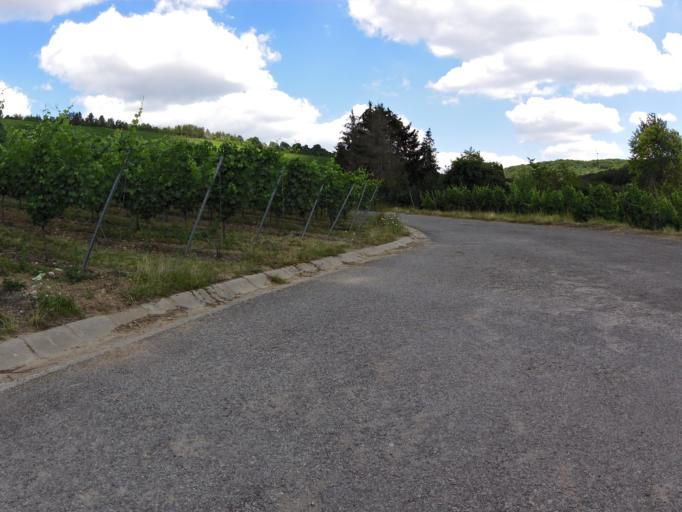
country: DE
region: Bavaria
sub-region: Regierungsbezirk Unterfranken
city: Thungersheim
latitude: 49.8810
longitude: 9.8605
